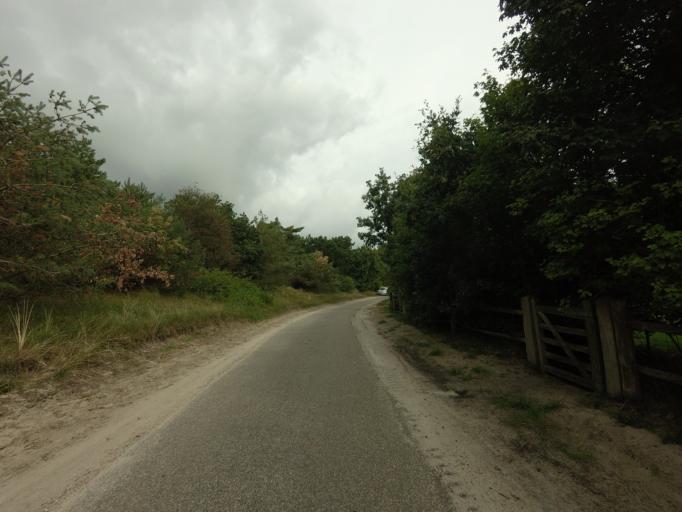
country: NL
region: Friesland
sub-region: Gemeente Ameland
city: Hollum
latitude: 53.4453
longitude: 5.6253
